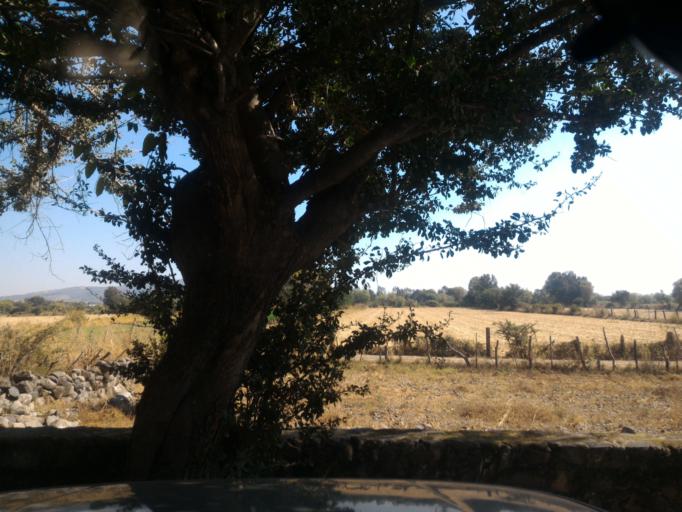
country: MX
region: Jalisco
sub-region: Poncitlan
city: Cuitzeo (La Estancia)
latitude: 20.3247
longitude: -102.7892
